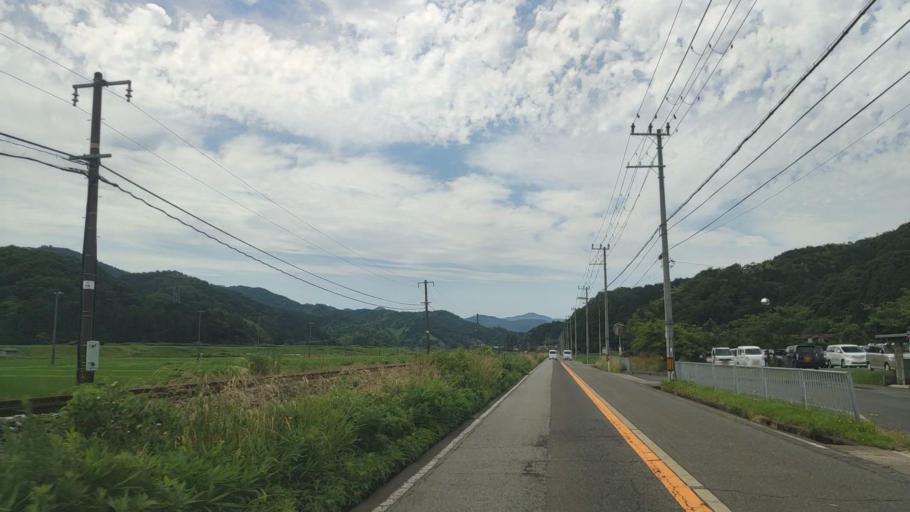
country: JP
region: Hyogo
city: Toyooka
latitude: 35.6404
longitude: 134.7579
